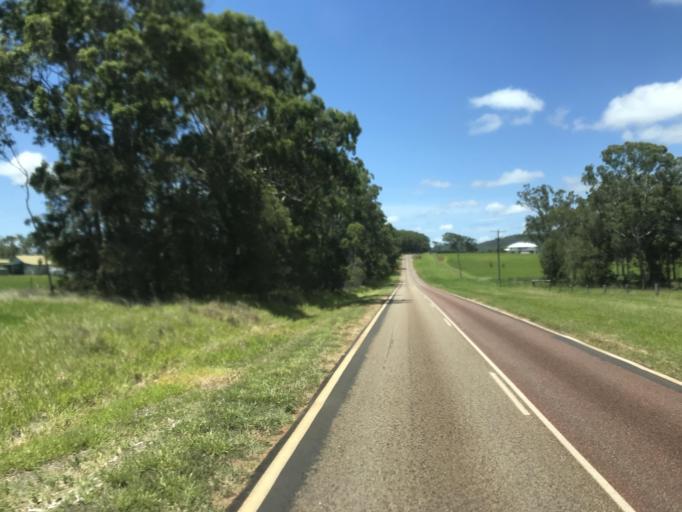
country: AU
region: Queensland
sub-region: Tablelands
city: Ravenshoe
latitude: -17.5189
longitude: 145.4516
